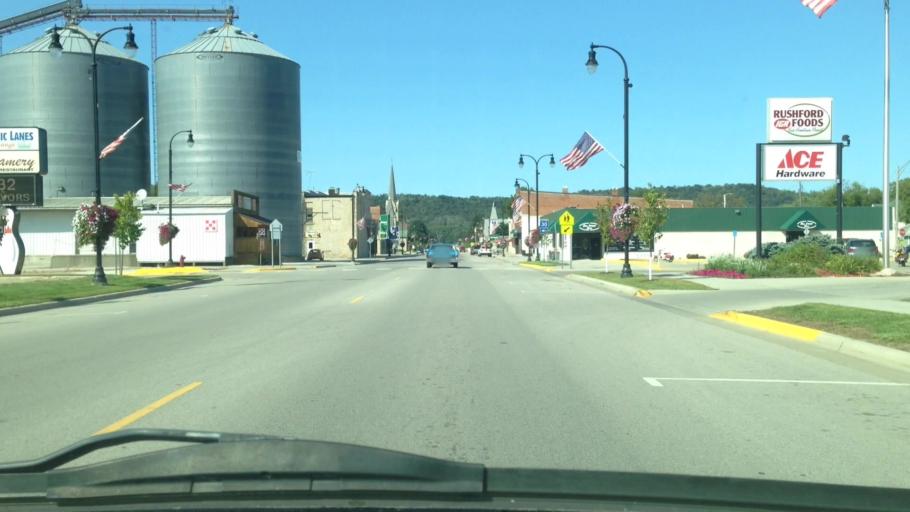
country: US
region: Minnesota
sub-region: Fillmore County
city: Rushford
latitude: 43.8067
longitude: -91.7532
